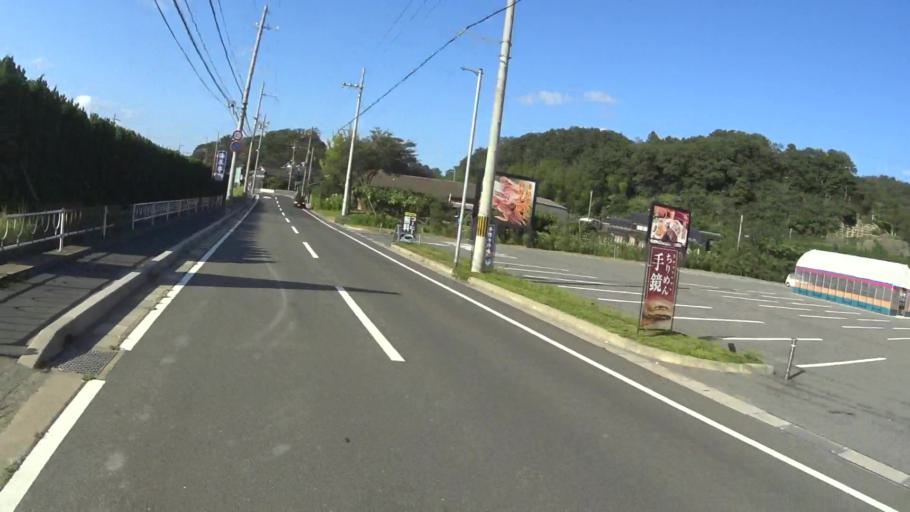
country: JP
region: Hyogo
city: Toyooka
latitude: 35.6524
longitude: 134.9698
